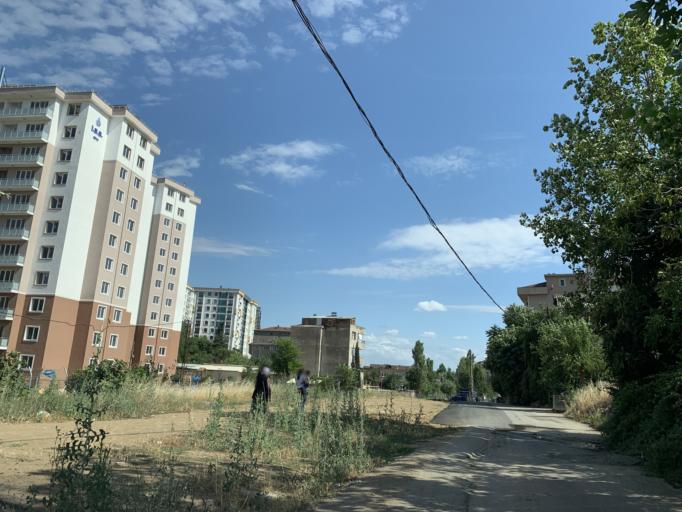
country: TR
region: Istanbul
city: Pendik
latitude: 40.8901
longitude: 29.2746
